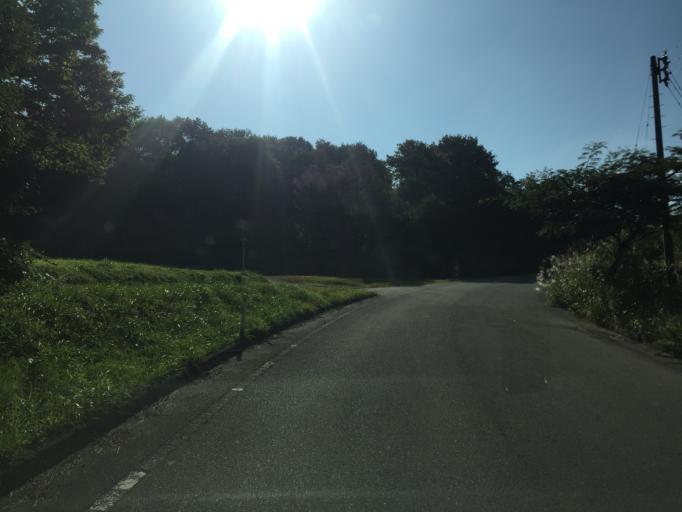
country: JP
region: Fukushima
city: Inawashiro
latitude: 37.4717
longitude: 139.9888
